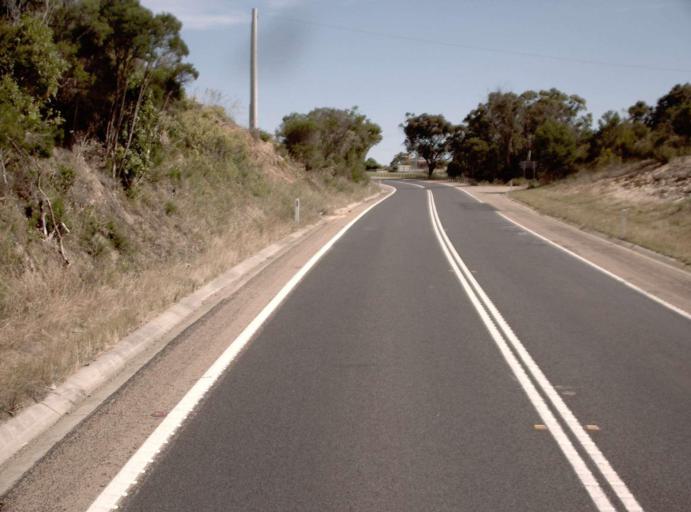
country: AU
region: Victoria
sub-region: East Gippsland
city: Lakes Entrance
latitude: -37.8624
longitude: 147.9525
